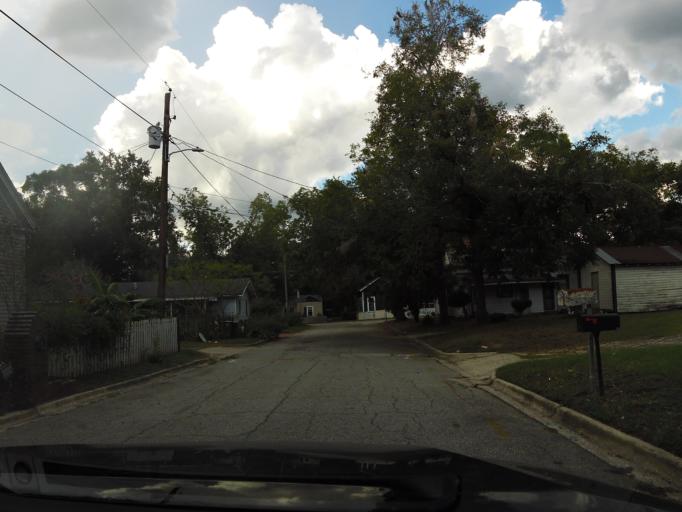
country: US
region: Georgia
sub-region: Lowndes County
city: Valdosta
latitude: 30.8317
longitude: -83.2860
